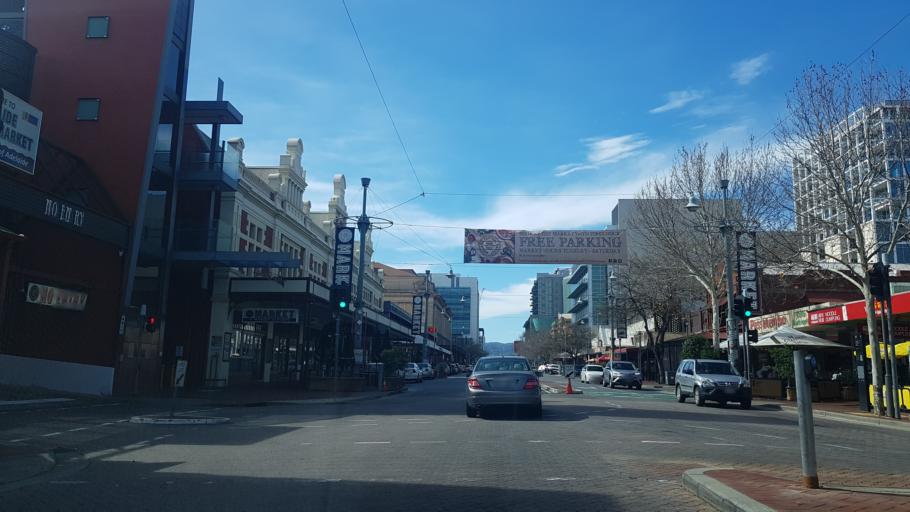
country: AU
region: South Australia
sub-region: Adelaide
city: Adelaide
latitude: -34.9303
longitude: 138.5969
